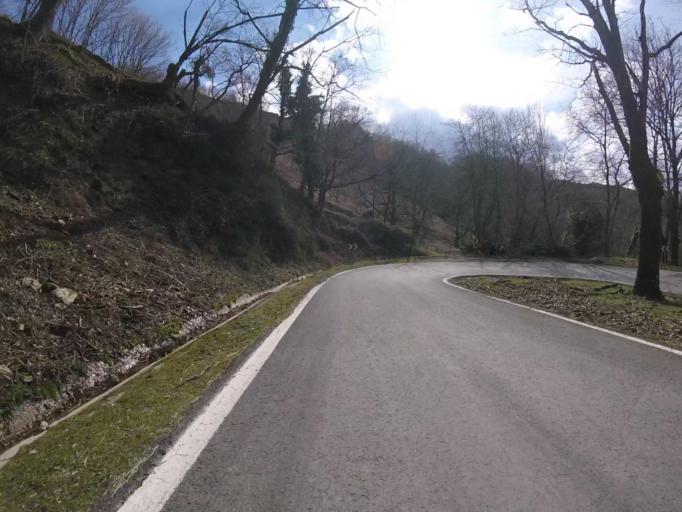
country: ES
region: Navarre
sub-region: Provincia de Navarra
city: Etxalar
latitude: 43.2522
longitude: -1.6122
